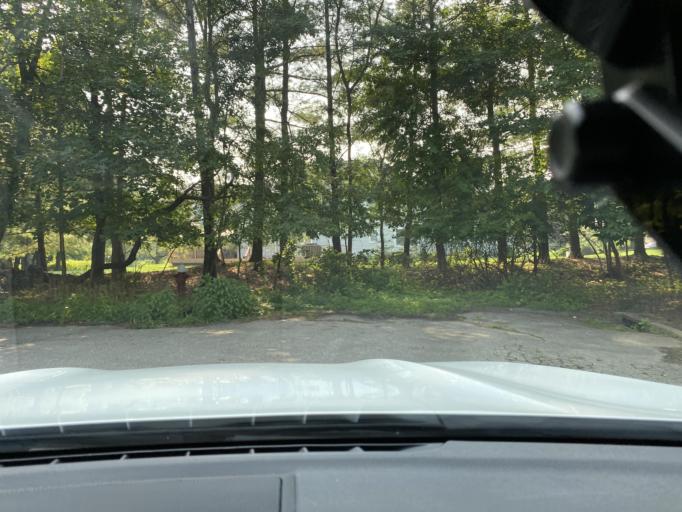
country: US
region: New York
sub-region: Rockland County
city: Airmont
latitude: 41.0869
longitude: -74.1204
